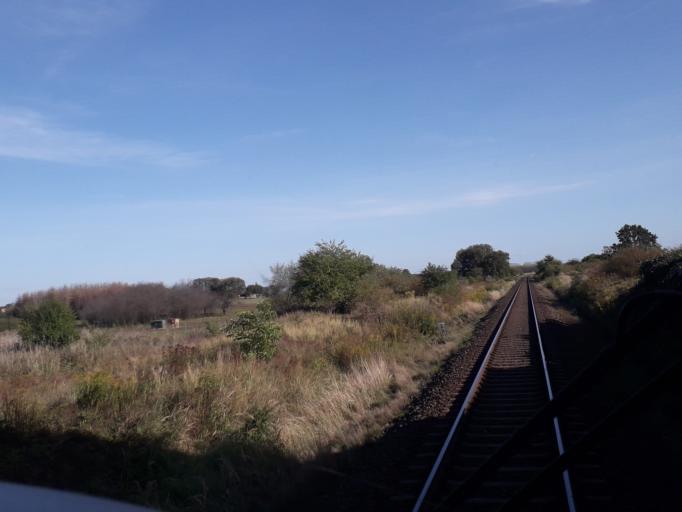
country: DE
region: Brandenburg
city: Velten
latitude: 52.7221
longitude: 13.1153
